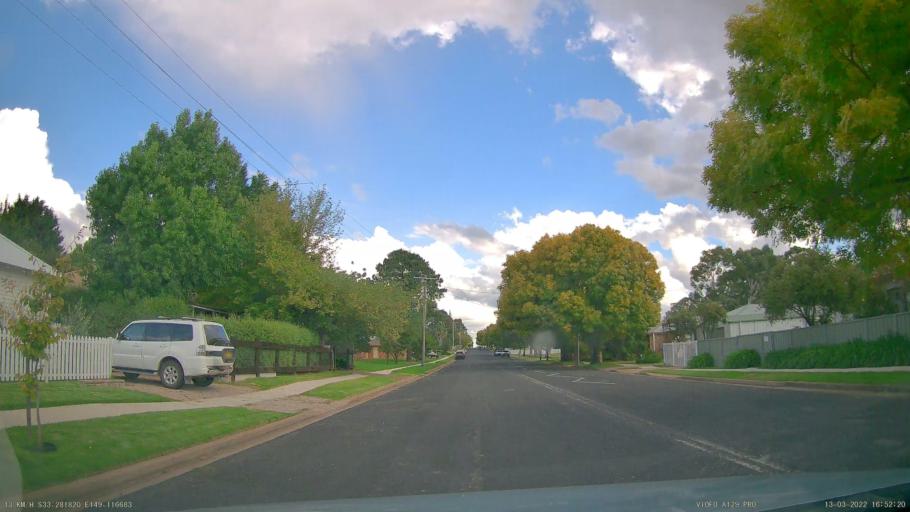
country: AU
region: New South Wales
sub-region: Orange Municipality
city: Orange
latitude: -33.2819
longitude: 149.1167
